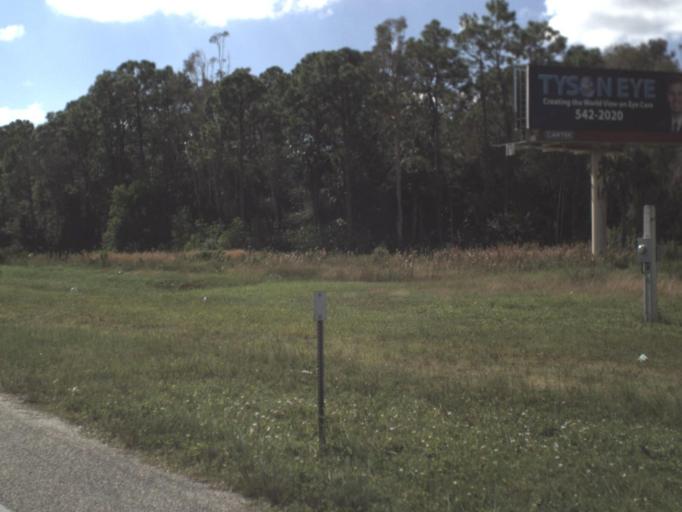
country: US
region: Florida
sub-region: Lee County
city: Suncoast Estates
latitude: 26.7327
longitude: -81.9107
